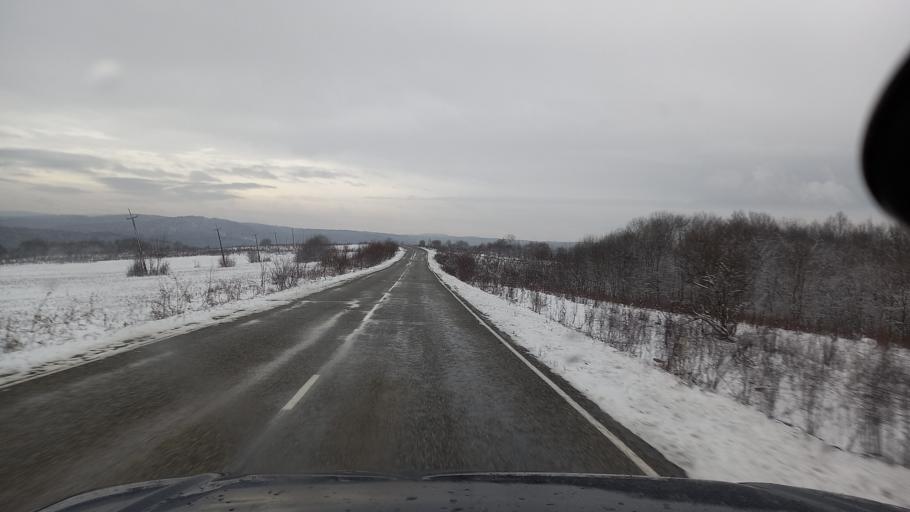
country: RU
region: Adygeya
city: Abadzekhskaya
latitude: 44.3587
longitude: 40.3787
